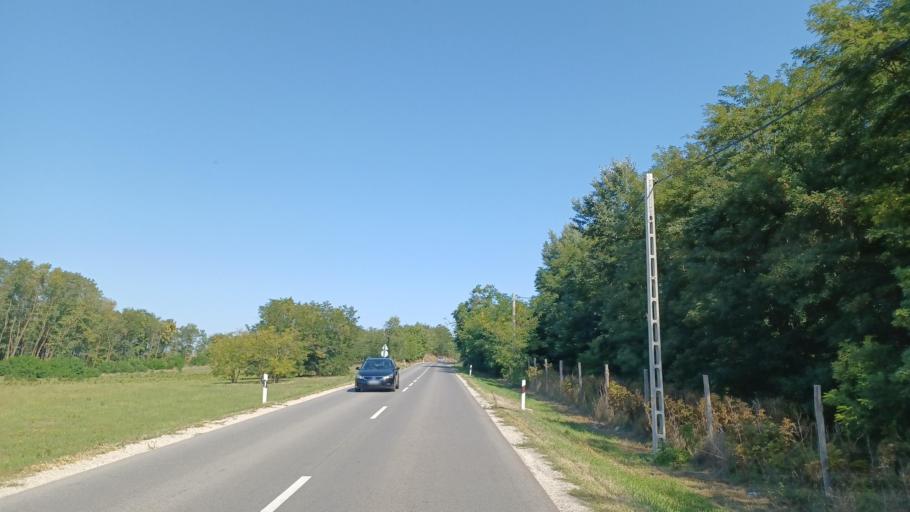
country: HU
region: Tolna
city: Nagydorog
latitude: 46.6810
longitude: 18.6683
